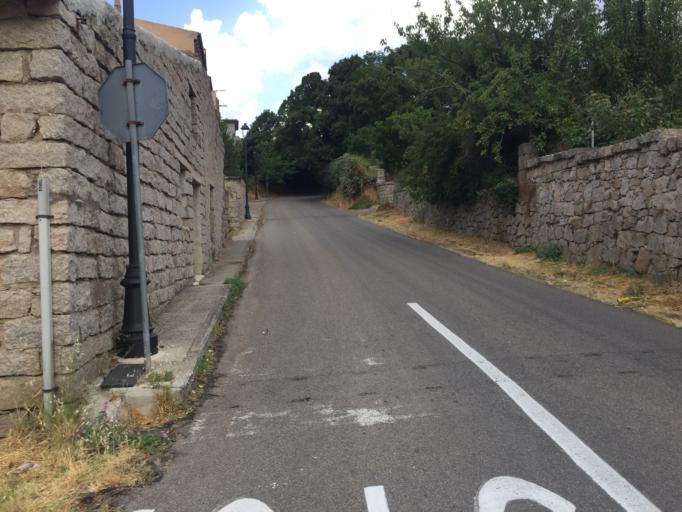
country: IT
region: Sardinia
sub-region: Provincia di Olbia-Tempio
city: Aggius
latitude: 40.9287
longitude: 9.0624
